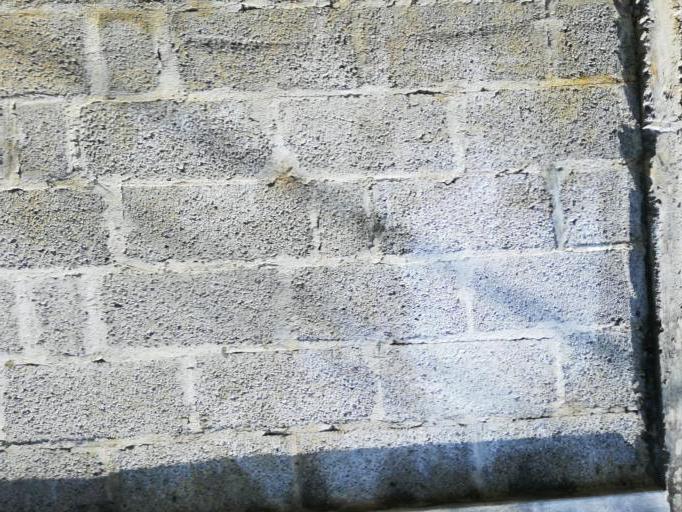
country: MU
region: Moka
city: Moka
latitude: -20.2244
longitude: 57.5071
